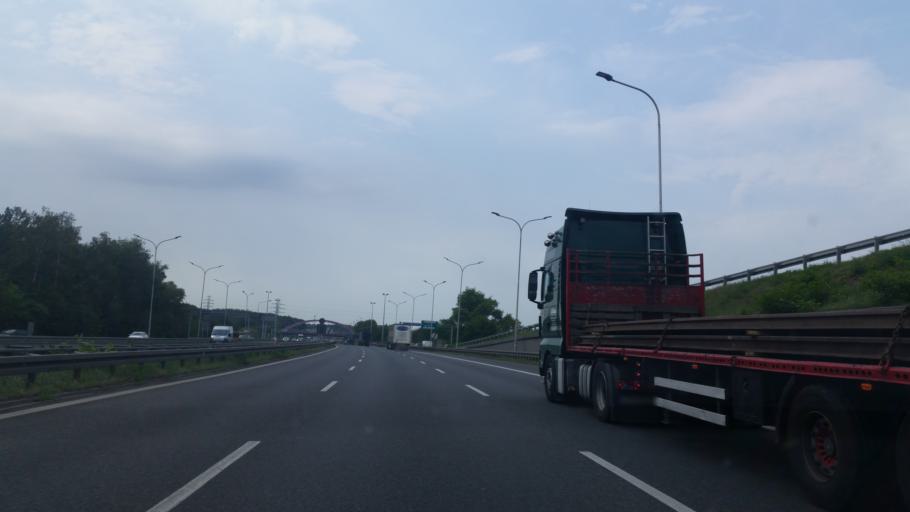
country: PL
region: Silesian Voivodeship
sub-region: Katowice
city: Katowice
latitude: 50.2507
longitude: 18.9978
